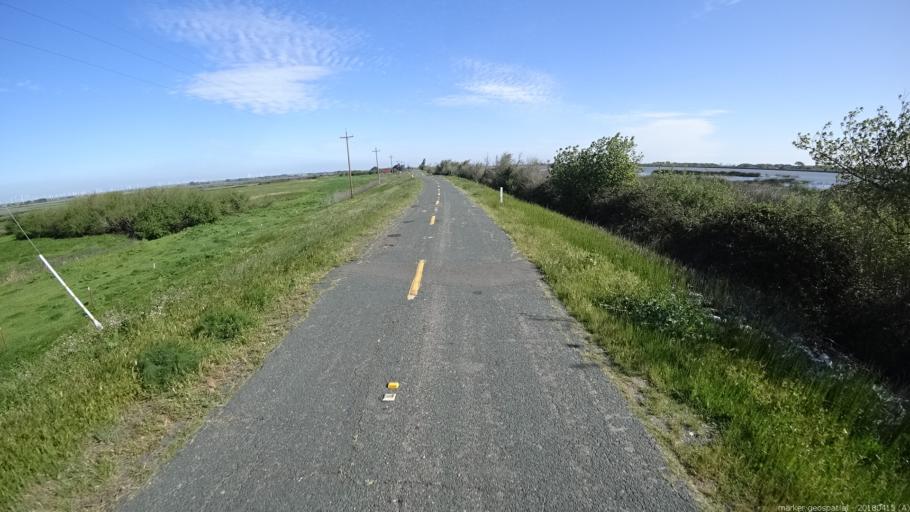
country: US
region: California
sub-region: Contra Costa County
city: Bethel Island
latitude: 38.0676
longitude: -121.6834
